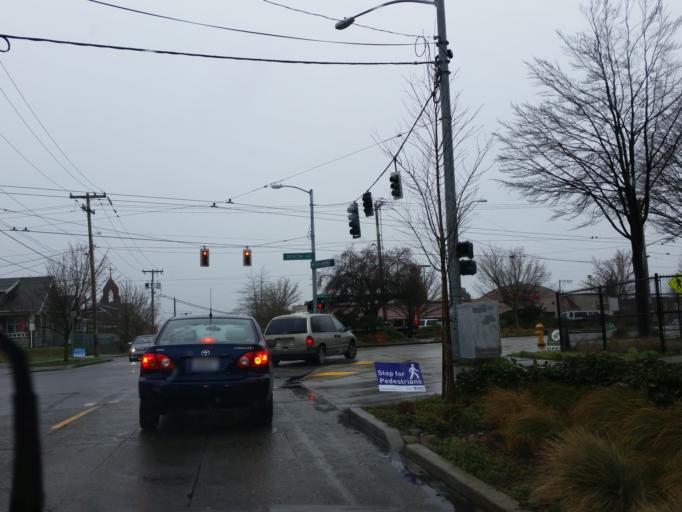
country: US
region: Washington
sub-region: King County
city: Seattle
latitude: 47.5786
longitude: -122.3112
